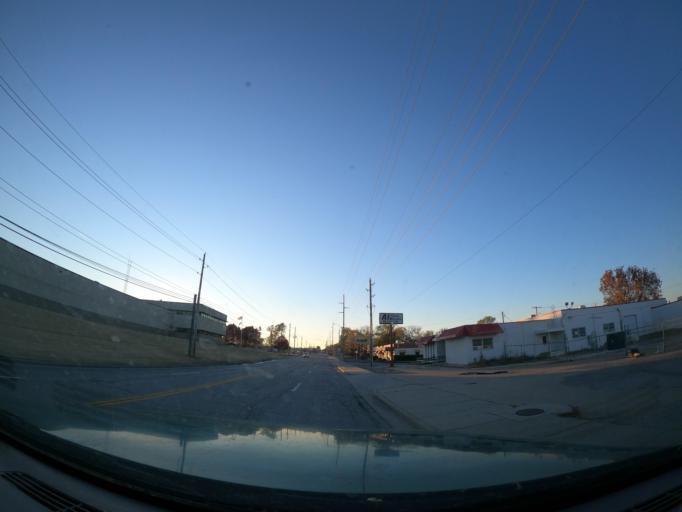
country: US
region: Oklahoma
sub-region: Tulsa County
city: Tulsa
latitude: 36.1407
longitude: -95.9107
